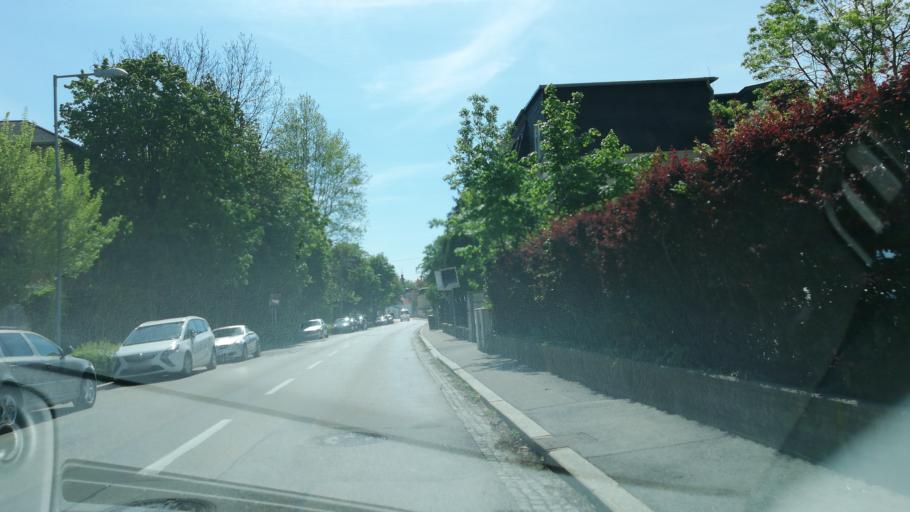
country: AT
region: Lower Austria
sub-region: Politischer Bezirk Baden
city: Baden
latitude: 48.0131
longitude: 16.2021
